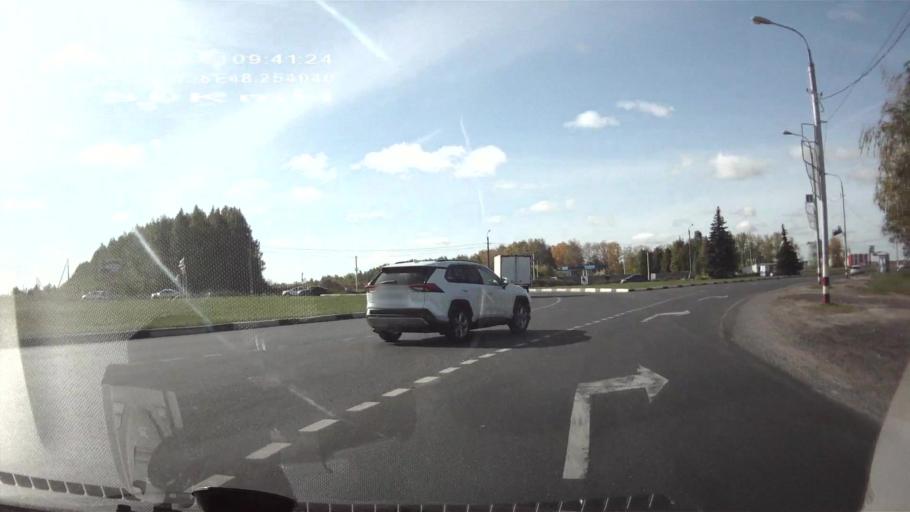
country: RU
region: Ulyanovsk
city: Isheyevka
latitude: 54.2913
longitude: 48.2539
